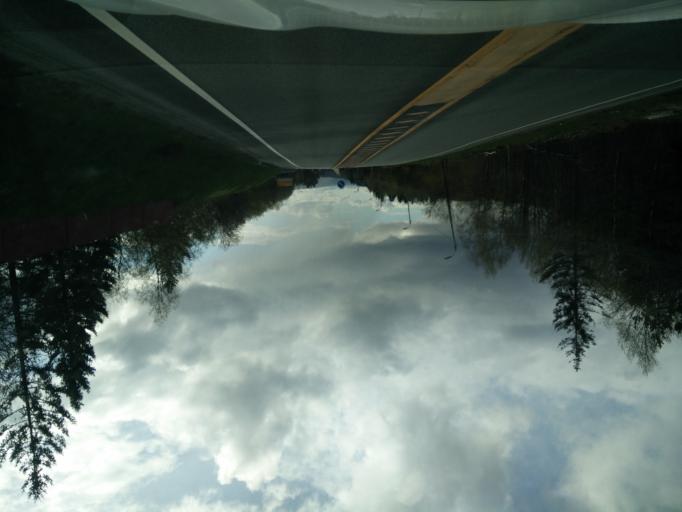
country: NO
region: Sor-Trondelag
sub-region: Trondheim
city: Trondheim
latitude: 63.3411
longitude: 10.3646
